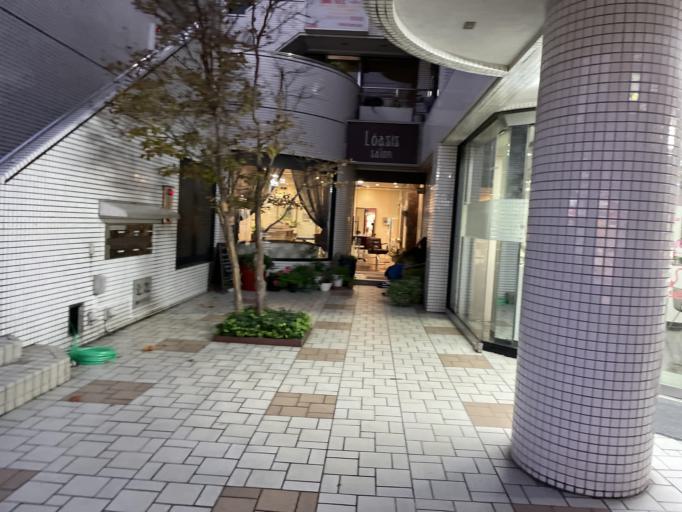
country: JP
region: Chiba
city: Nagareyama
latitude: 35.8237
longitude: 139.9148
